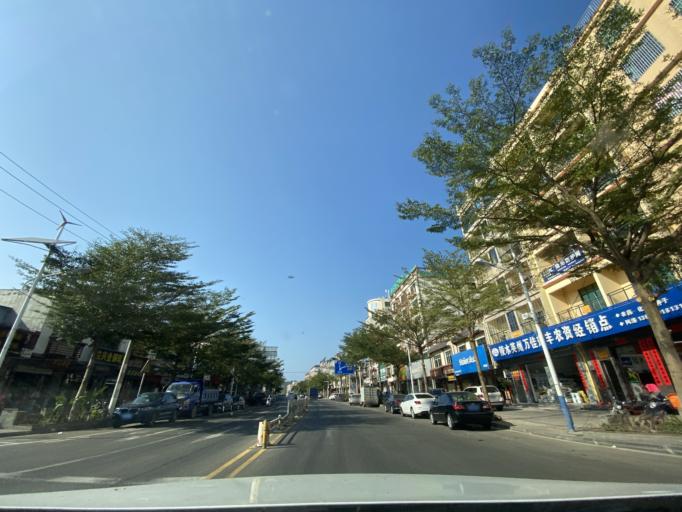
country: CN
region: Hainan
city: Yingzhou
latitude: 18.4271
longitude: 109.8547
